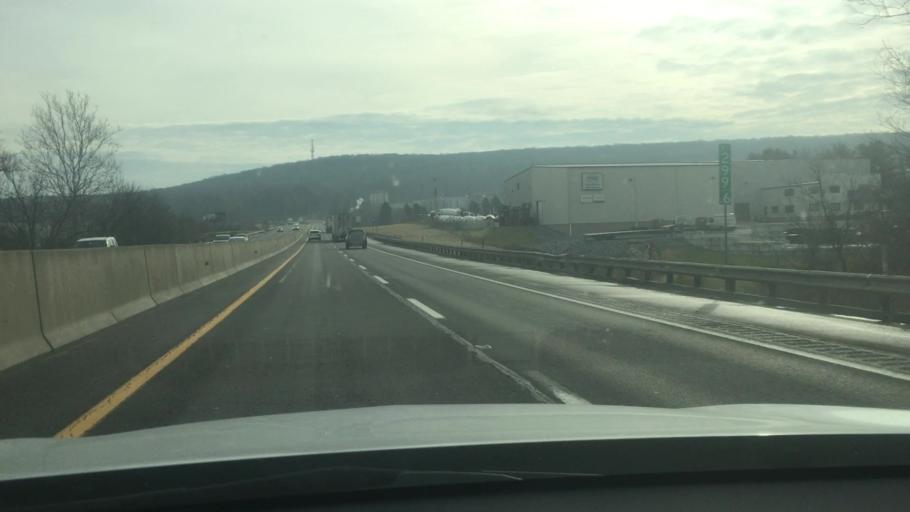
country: US
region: Pennsylvania
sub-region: Chester County
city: Elverson
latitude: 40.1515
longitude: -75.8621
